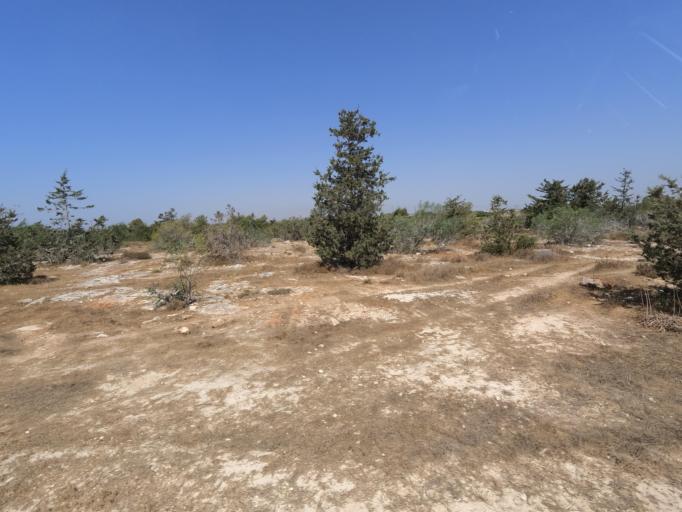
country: CY
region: Ammochostos
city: Paralimni
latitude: 35.0115
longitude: 33.9675
